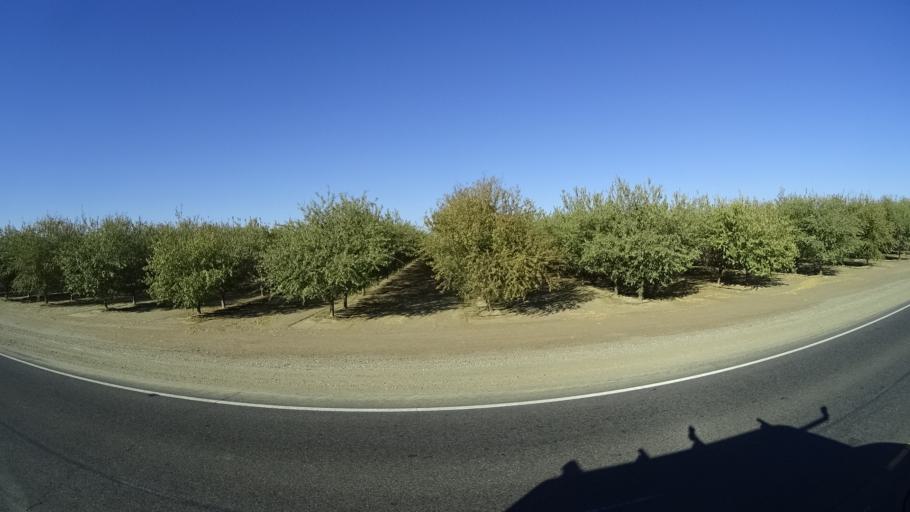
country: US
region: California
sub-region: Kern County
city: Greenfield
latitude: 35.2671
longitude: -119.1163
